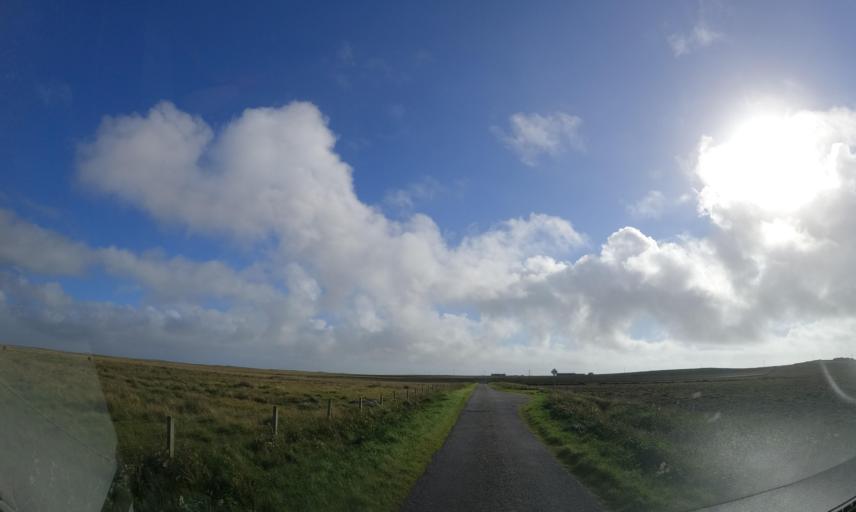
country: GB
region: Scotland
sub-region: Eilean Siar
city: Barra
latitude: 56.4831
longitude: -6.9286
